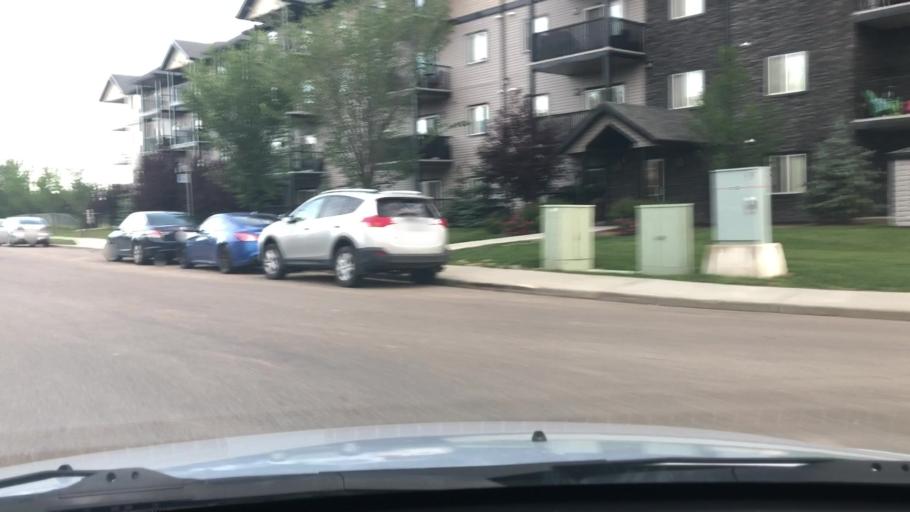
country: CA
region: Alberta
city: Edmonton
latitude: 53.6104
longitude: -113.5381
